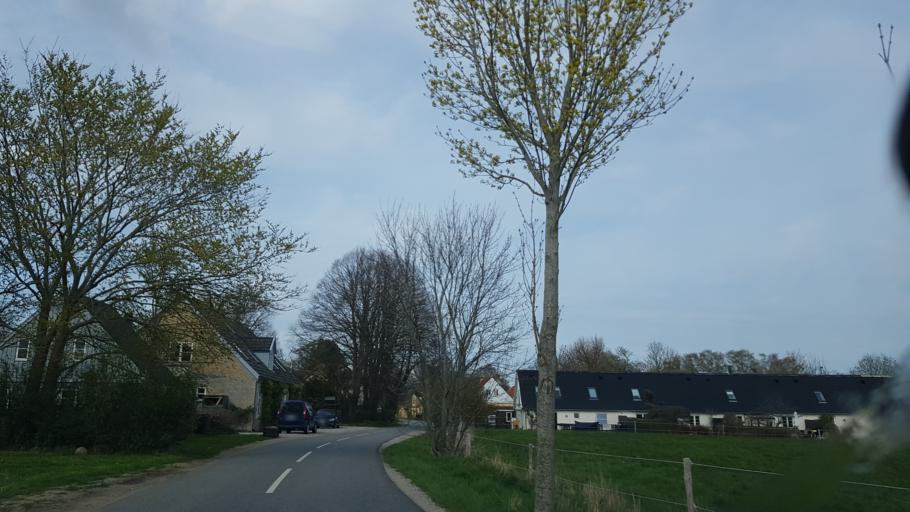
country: DK
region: Capital Region
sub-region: Allerod Kommune
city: Lynge
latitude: 55.8714
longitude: 12.2987
